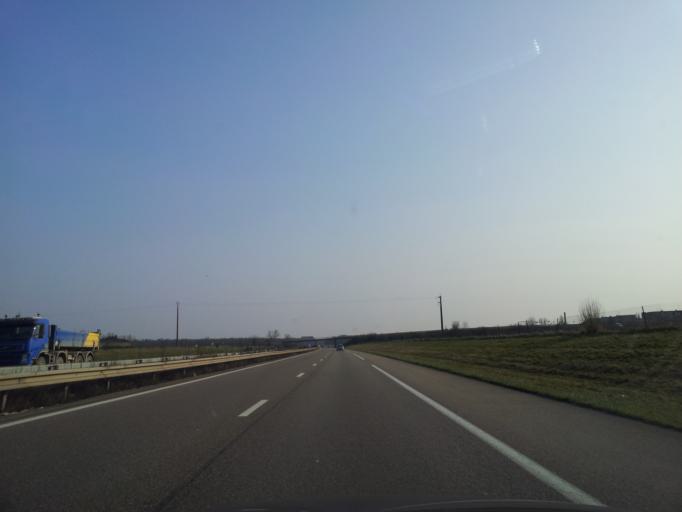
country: FR
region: Alsace
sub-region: Departement du Haut-Rhin
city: Habsheim
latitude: 47.7315
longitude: 7.4262
